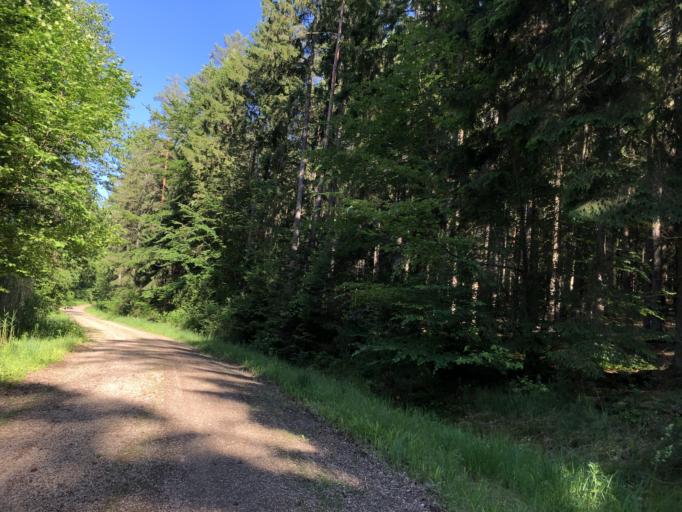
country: DE
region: Bavaria
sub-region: Upper Franconia
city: Memmelsdorf
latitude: 49.9172
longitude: 10.9693
